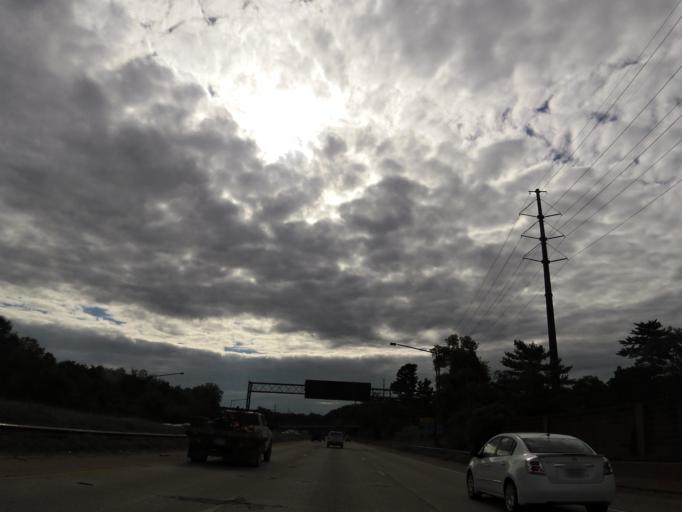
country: US
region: Tennessee
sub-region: Davidson County
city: Oak Hill
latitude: 36.1163
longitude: -86.7881
